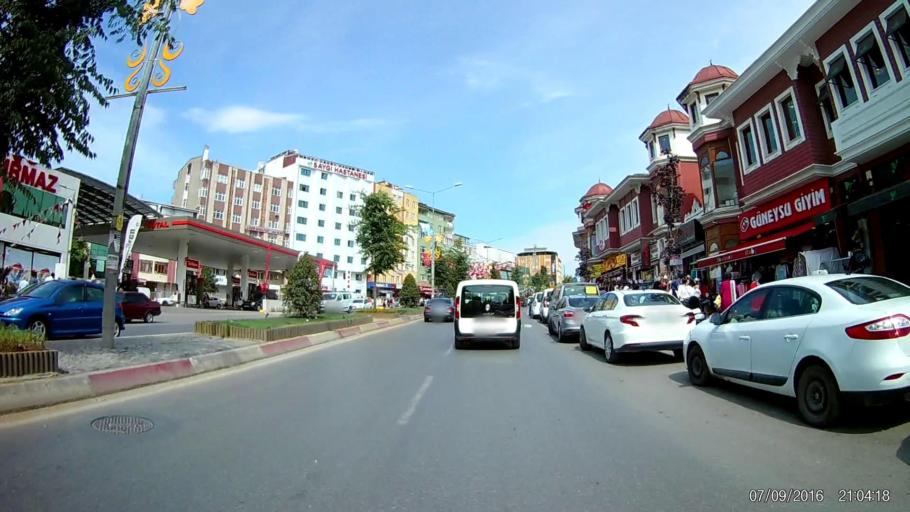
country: TR
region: Istanbul
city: Sultanbeyli
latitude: 40.9692
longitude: 29.2570
